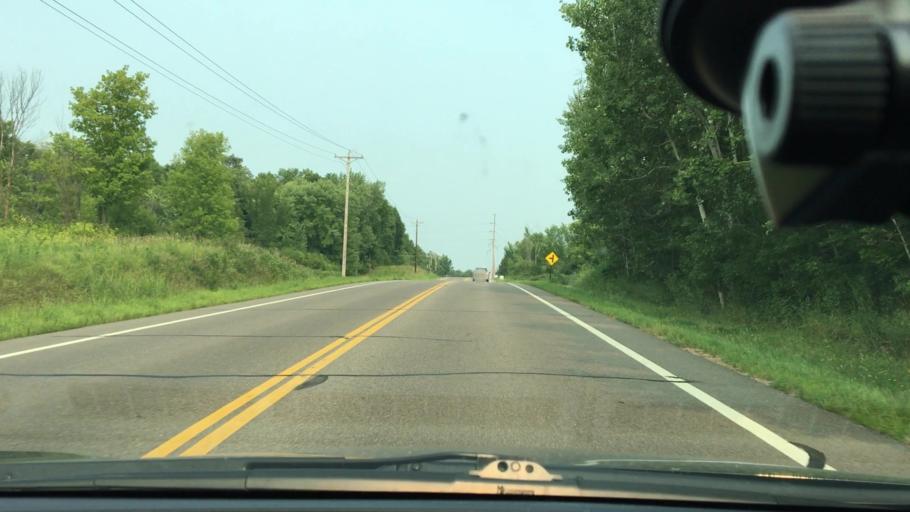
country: US
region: Minnesota
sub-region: Hennepin County
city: Champlin
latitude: 45.1882
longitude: -93.4454
